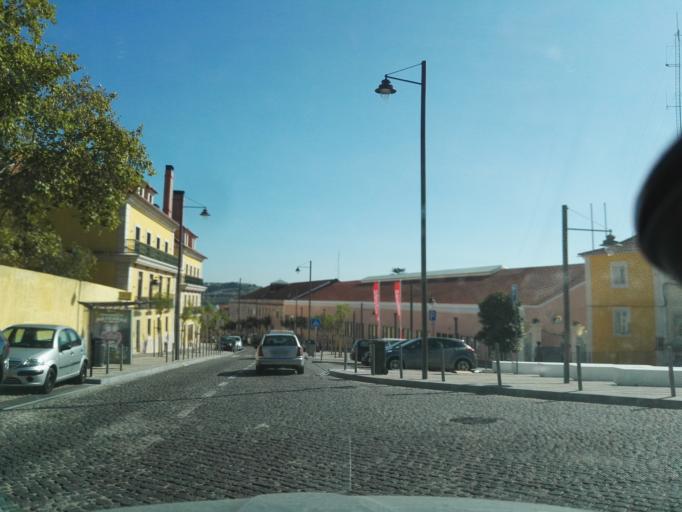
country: PT
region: Lisbon
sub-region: Oeiras
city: Alges
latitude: 38.7009
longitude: -9.1998
